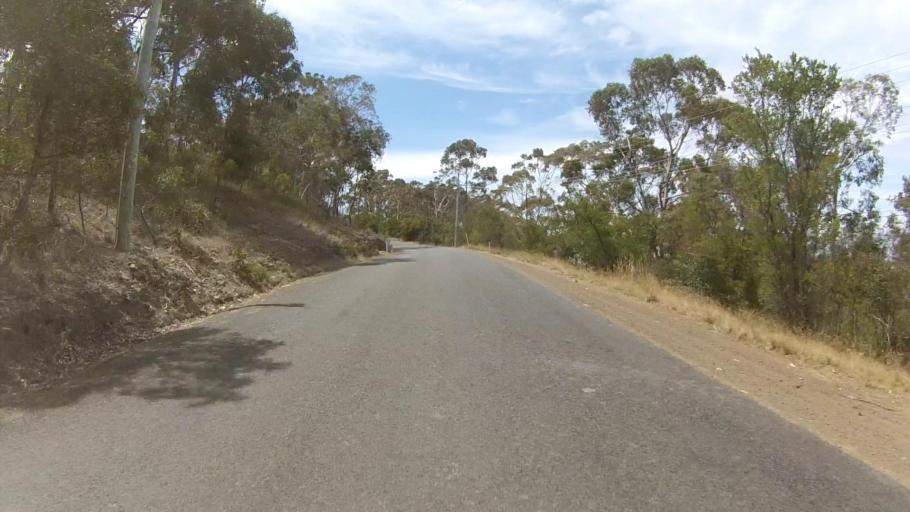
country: AU
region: Tasmania
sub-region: Kingborough
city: Blackmans Bay
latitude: -43.0526
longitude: 147.3388
